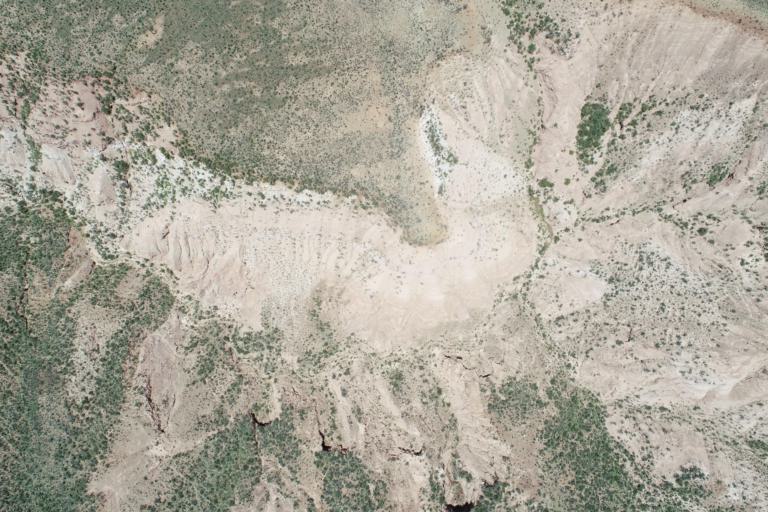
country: BO
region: La Paz
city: Curahuara de Carangas
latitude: -17.3088
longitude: -68.5055
